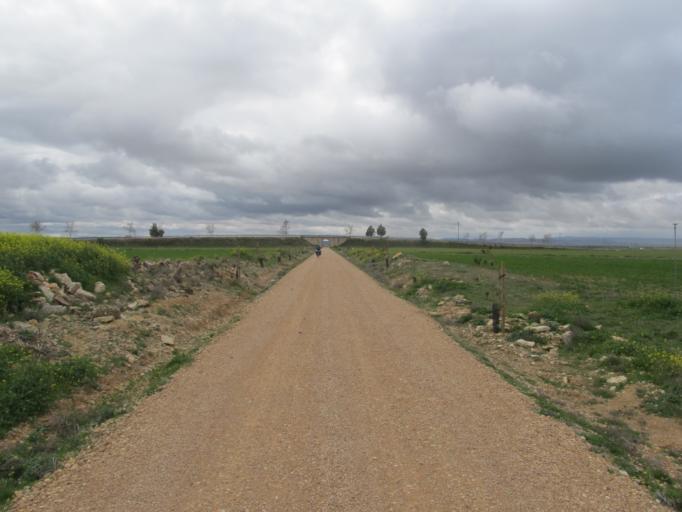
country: ES
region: Castille-La Mancha
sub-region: Provincia de Albacete
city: Albacete
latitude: 38.9502
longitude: -1.9788
